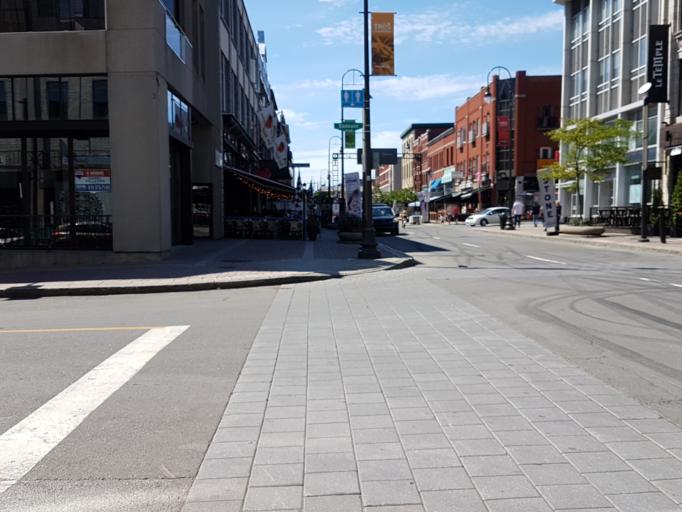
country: CA
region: Quebec
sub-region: Mauricie
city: Trois-Rivieres
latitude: 46.3421
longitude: -72.5417
